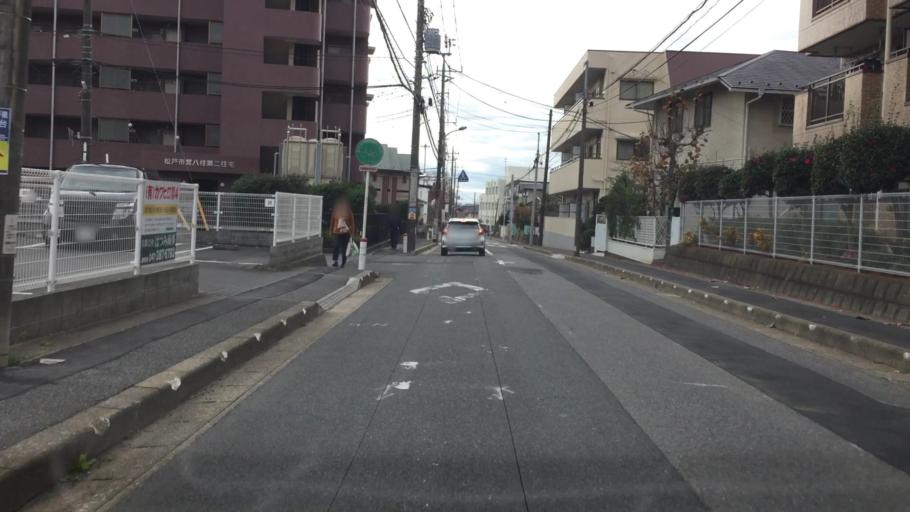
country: JP
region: Chiba
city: Matsudo
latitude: 35.7896
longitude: 139.9372
